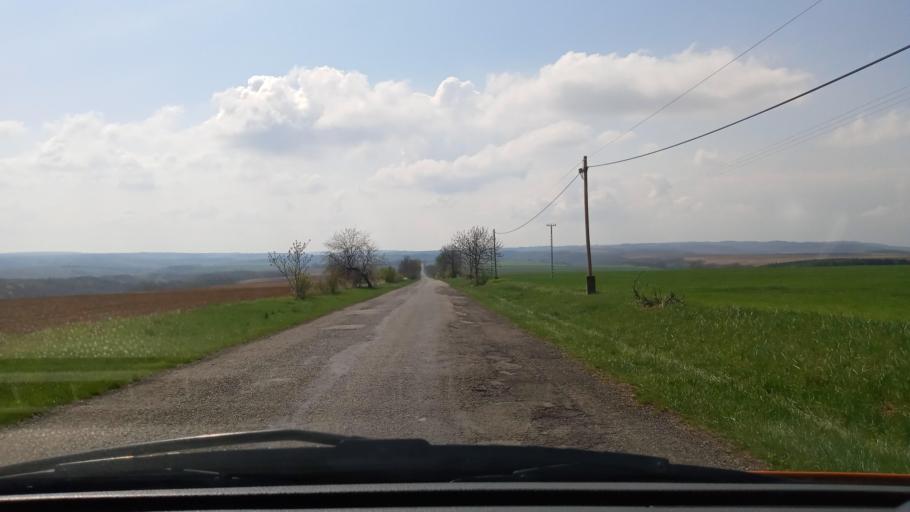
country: HU
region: Baranya
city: Pecsvarad
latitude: 46.1018
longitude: 18.4968
